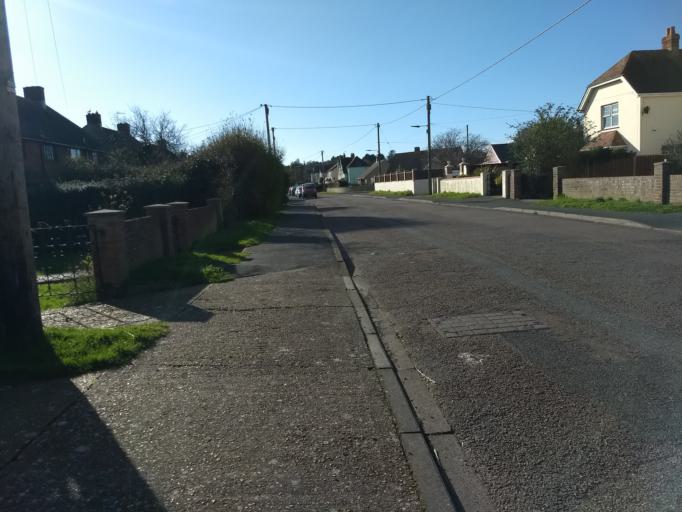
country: GB
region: England
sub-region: Isle of Wight
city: Bembridge
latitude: 50.6828
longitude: -1.0802
